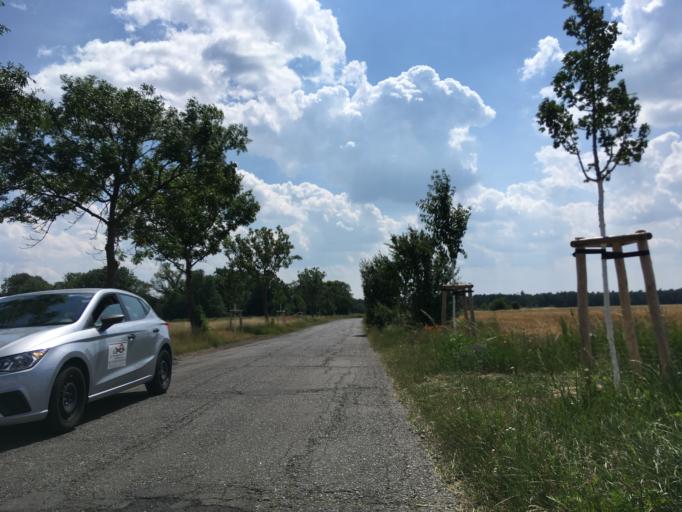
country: DE
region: Brandenburg
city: Rudnitz
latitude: 52.6786
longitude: 13.6527
